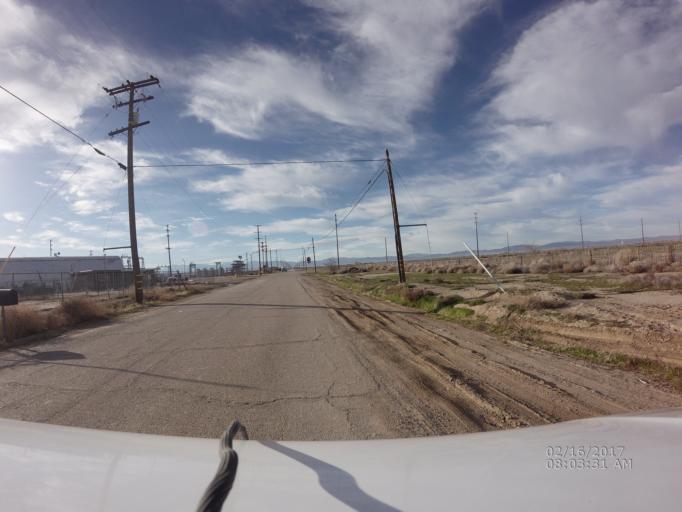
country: US
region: California
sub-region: Kern County
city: Edwards Air Force Base
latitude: 34.7645
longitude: -117.9699
